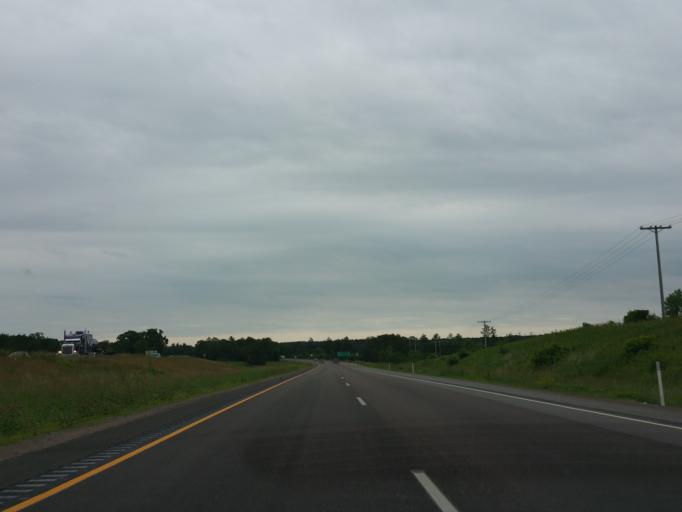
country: US
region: Wisconsin
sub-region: Trempealeau County
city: Osseo
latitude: 44.5749
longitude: -91.2021
